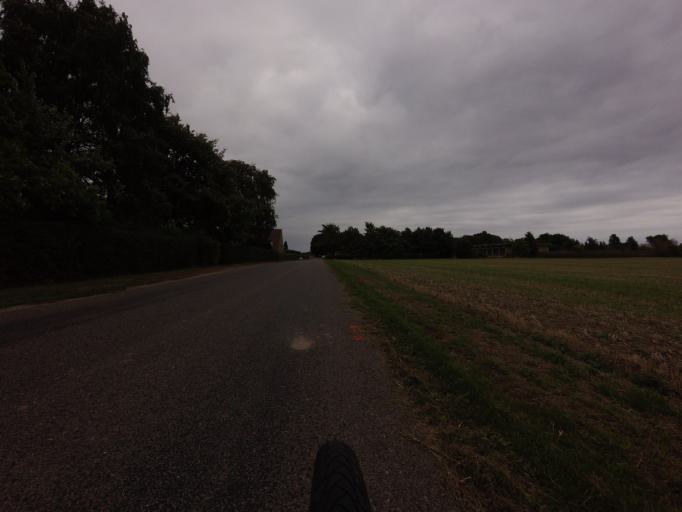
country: DK
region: Zealand
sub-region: Stevns Kommune
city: Store Heddinge
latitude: 55.3284
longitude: 12.4476
